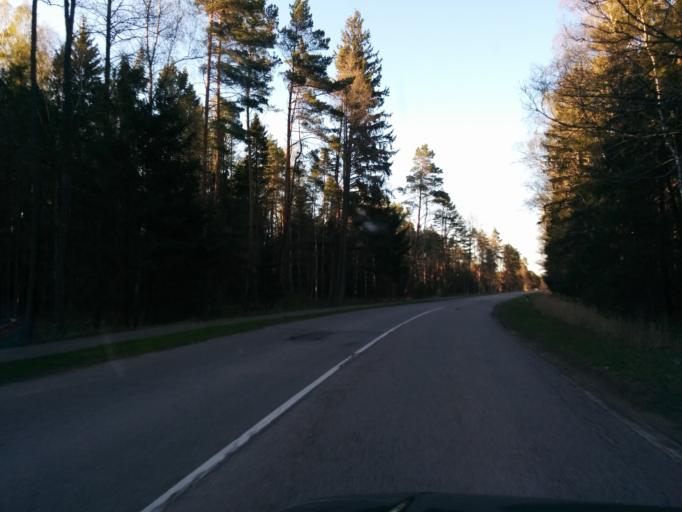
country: LV
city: Tireli
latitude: 56.9606
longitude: 23.5236
